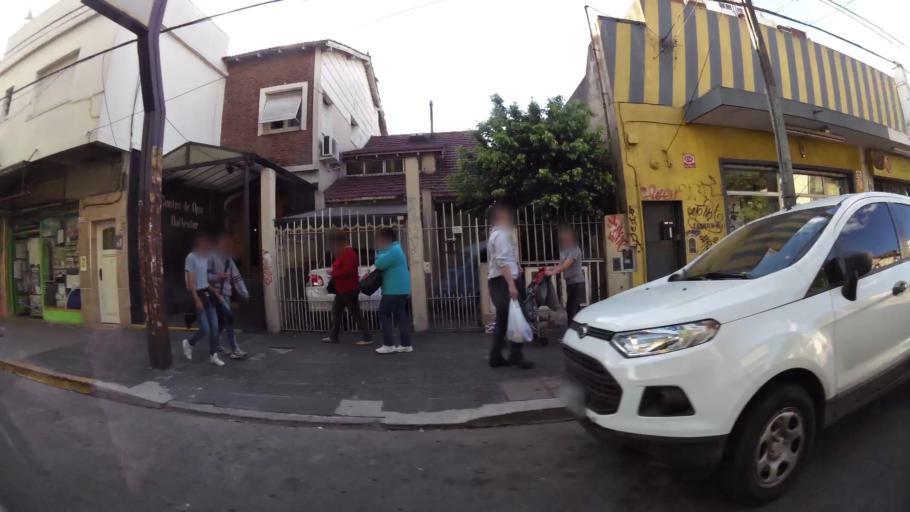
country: AR
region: Buenos Aires
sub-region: Partido de General San Martin
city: General San Martin
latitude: -34.5510
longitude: -58.5533
